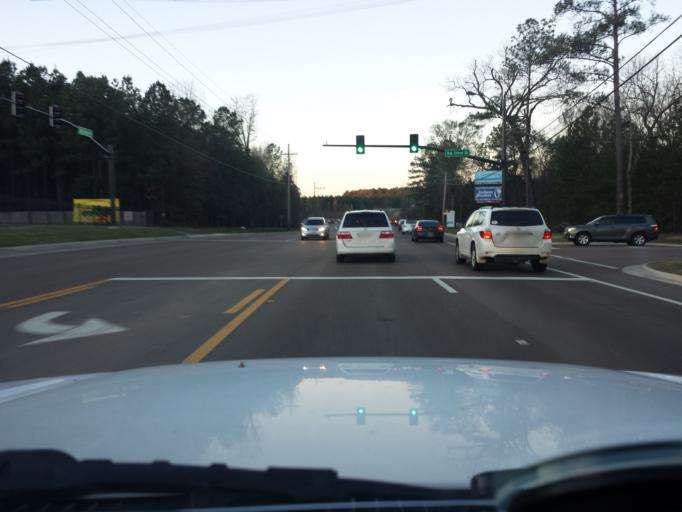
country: US
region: Mississippi
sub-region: Madison County
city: Ridgeland
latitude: 32.3714
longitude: -90.0517
